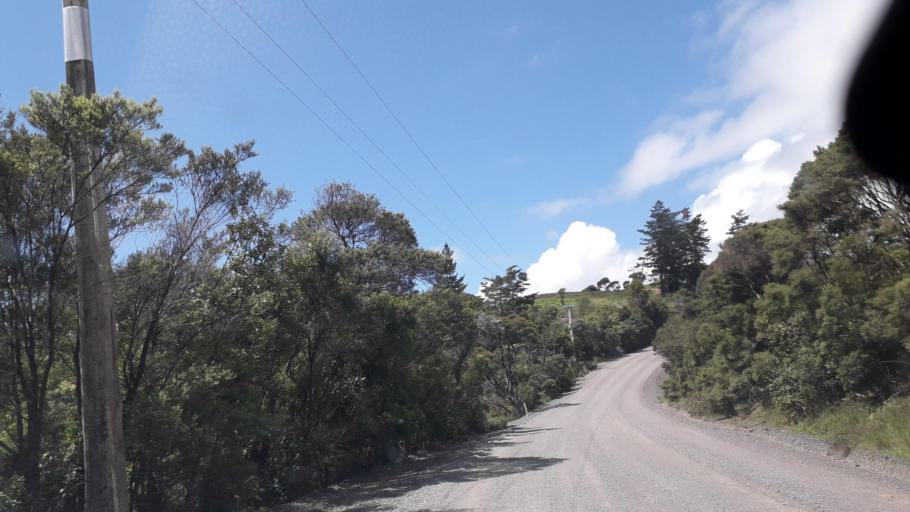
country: NZ
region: Northland
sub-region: Far North District
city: Paihia
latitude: -35.2384
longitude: 174.2494
